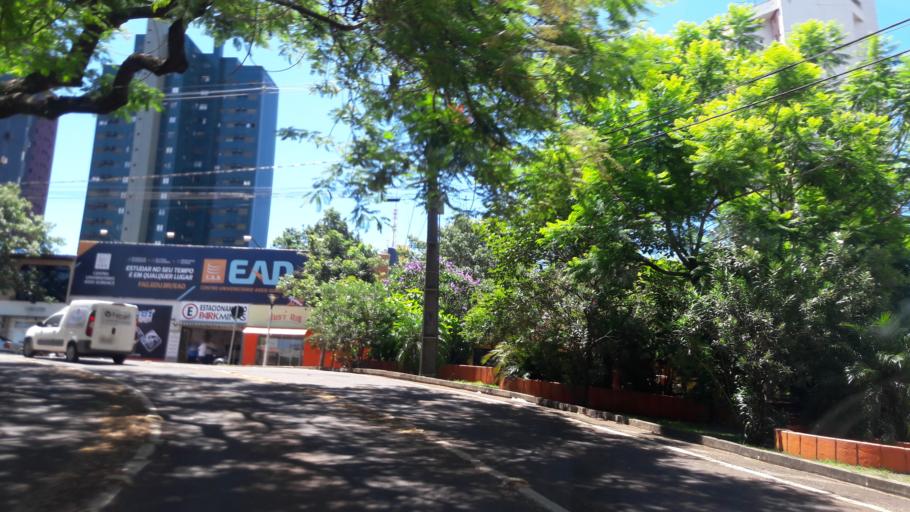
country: BR
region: Parana
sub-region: Cascavel
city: Cascavel
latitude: -24.9525
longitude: -53.4574
